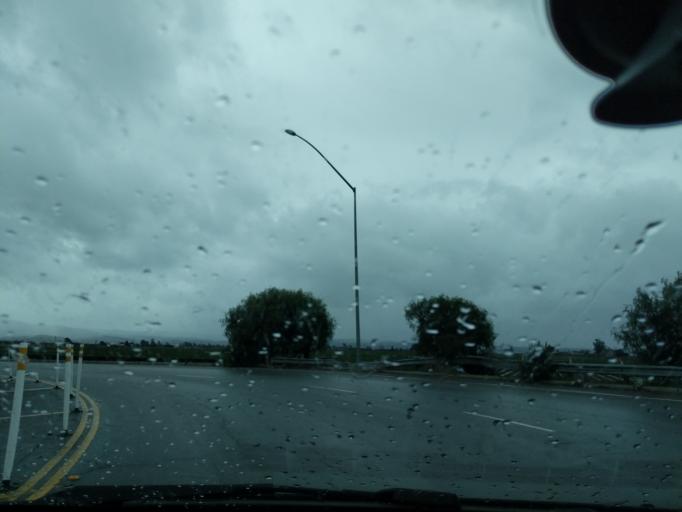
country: US
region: California
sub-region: Monterey County
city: Boronda
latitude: 36.7191
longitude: -121.6688
